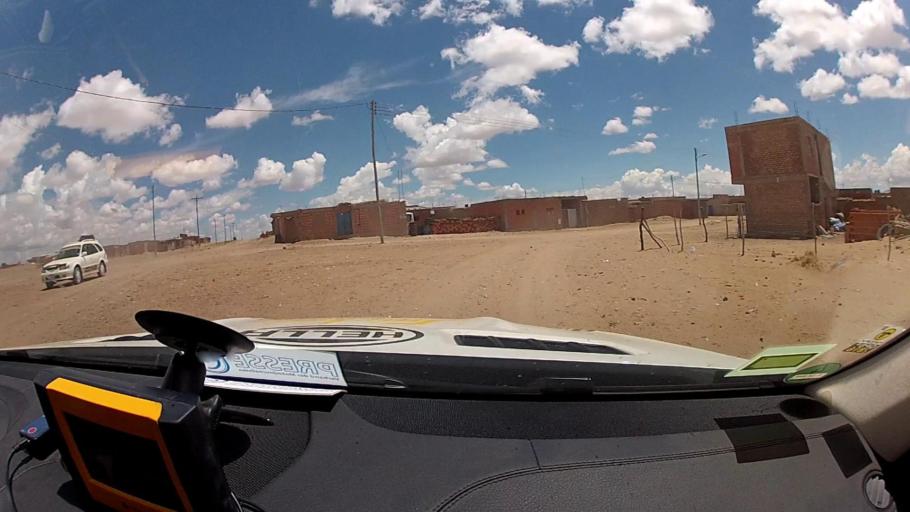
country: BO
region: Potosi
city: Villazon
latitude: -22.0805
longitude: -65.6100
